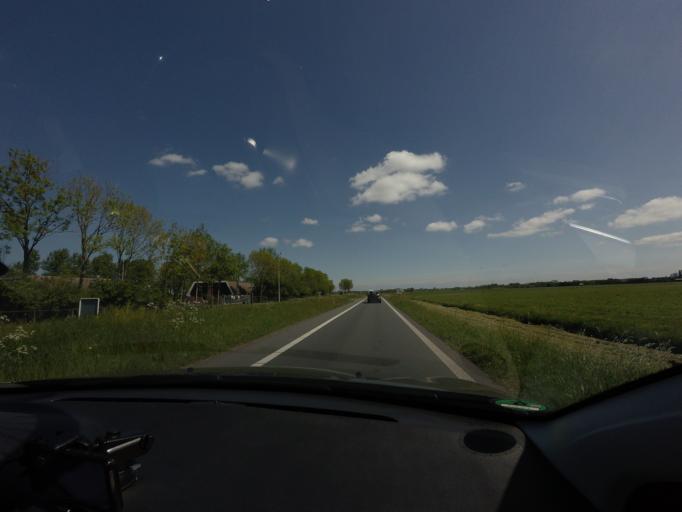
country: NL
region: North Holland
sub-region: Gemeente Beemster
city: Halfweg
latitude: 52.5387
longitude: 4.9080
